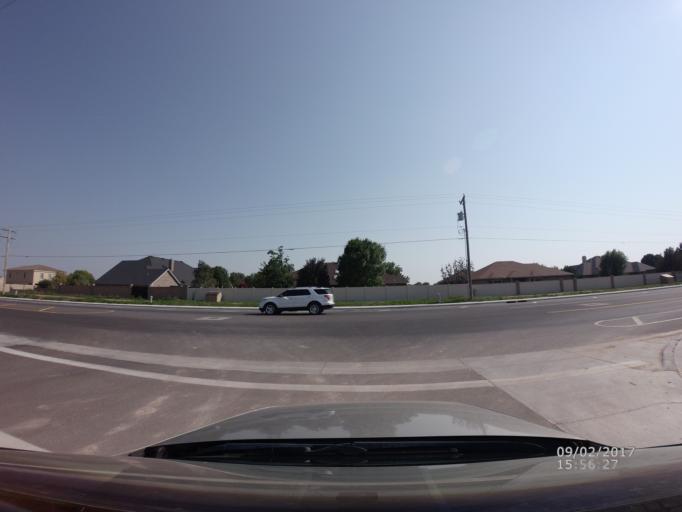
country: US
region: New Mexico
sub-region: Curry County
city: Clovis
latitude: 34.4484
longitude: -103.1883
